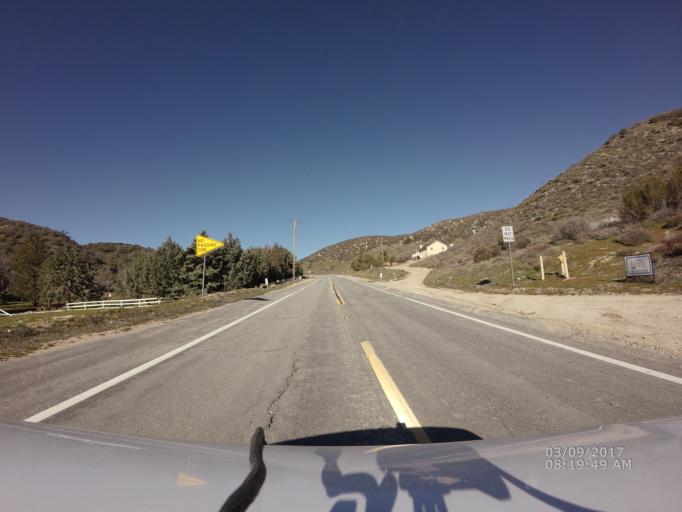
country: US
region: California
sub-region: Los Angeles County
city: Leona Valley
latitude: 34.6590
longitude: -118.3470
